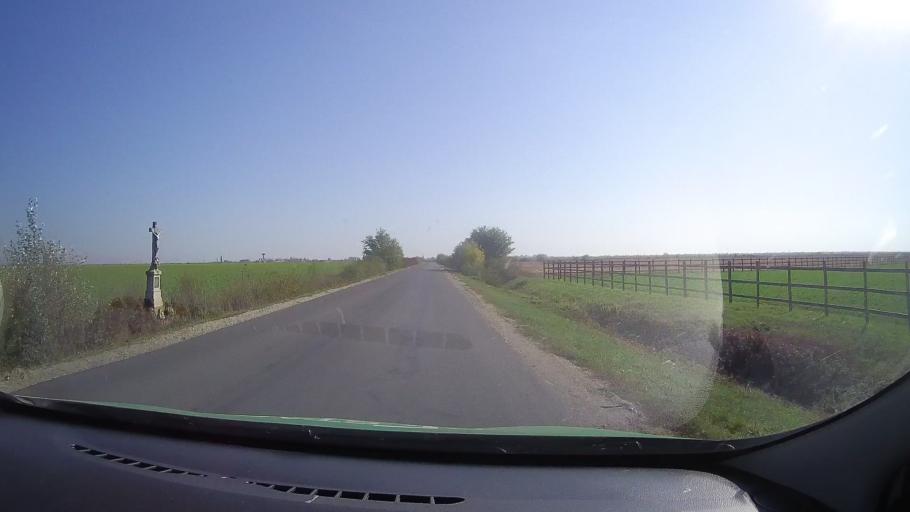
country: RO
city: Foieni
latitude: 47.6938
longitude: 22.4162
